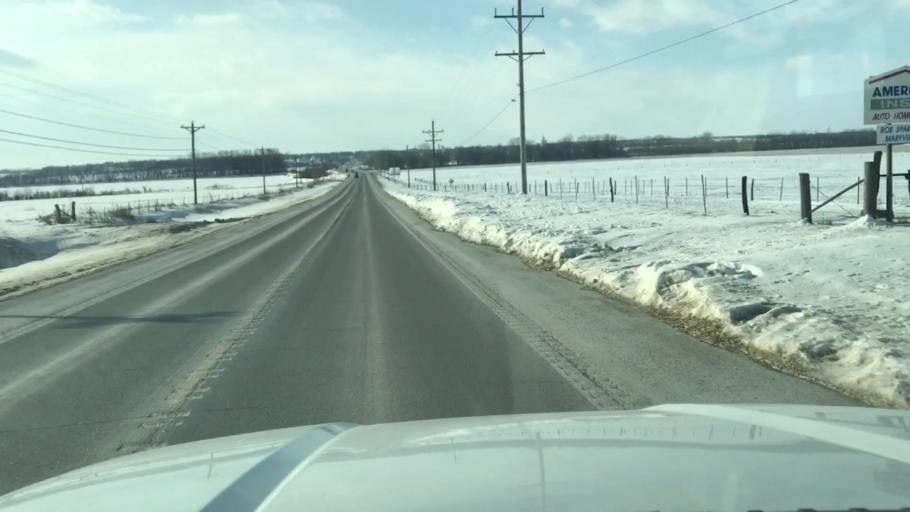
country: US
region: Missouri
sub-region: Nodaway County
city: Maryville
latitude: 40.3448
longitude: -94.8196
